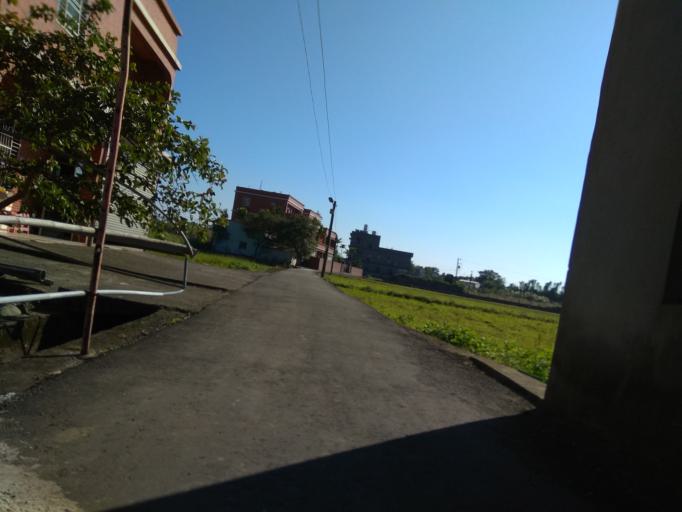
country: TW
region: Taiwan
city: Taoyuan City
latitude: 24.9944
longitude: 121.1987
